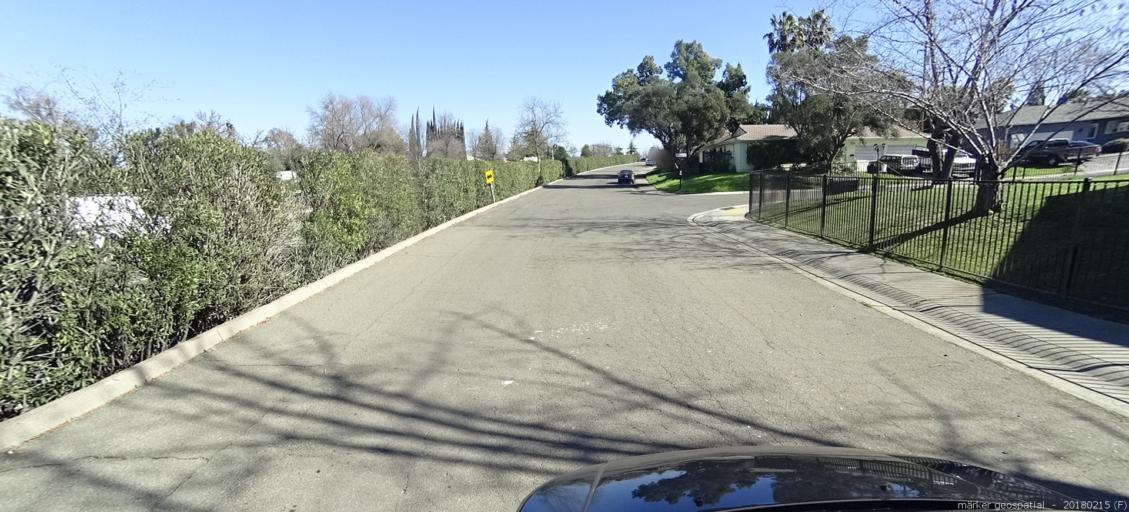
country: US
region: California
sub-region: Sacramento County
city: Foothill Farms
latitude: 38.6631
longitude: -121.3204
